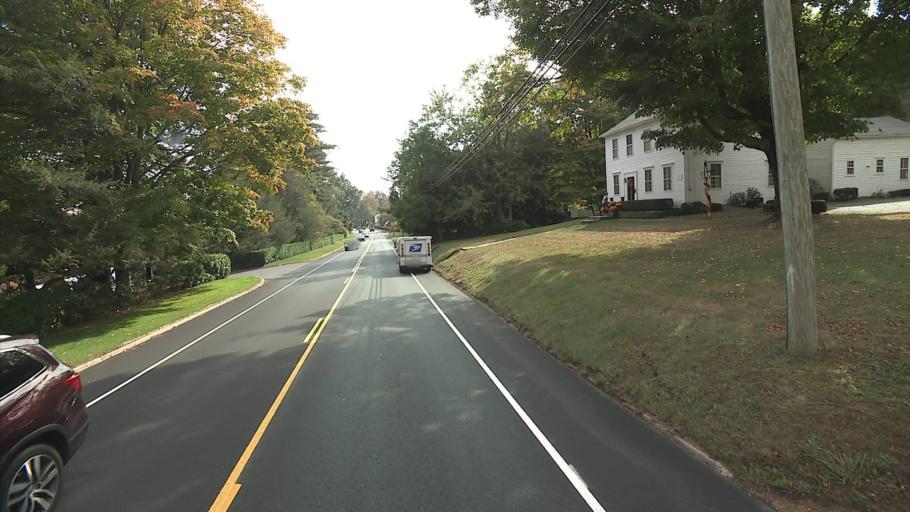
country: US
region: Connecticut
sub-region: Litchfield County
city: Watertown
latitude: 41.6034
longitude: -73.1258
